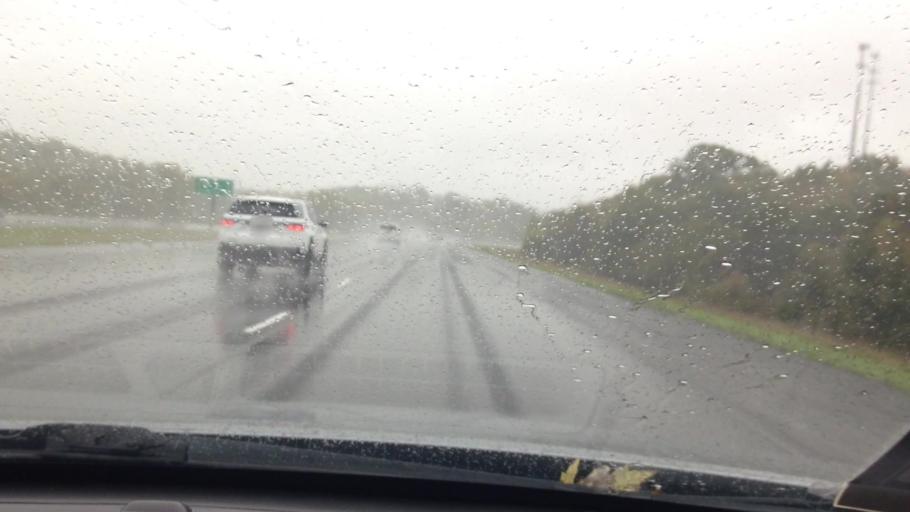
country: US
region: Kansas
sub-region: Wyandotte County
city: Edwardsville
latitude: 39.1671
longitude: -94.8139
